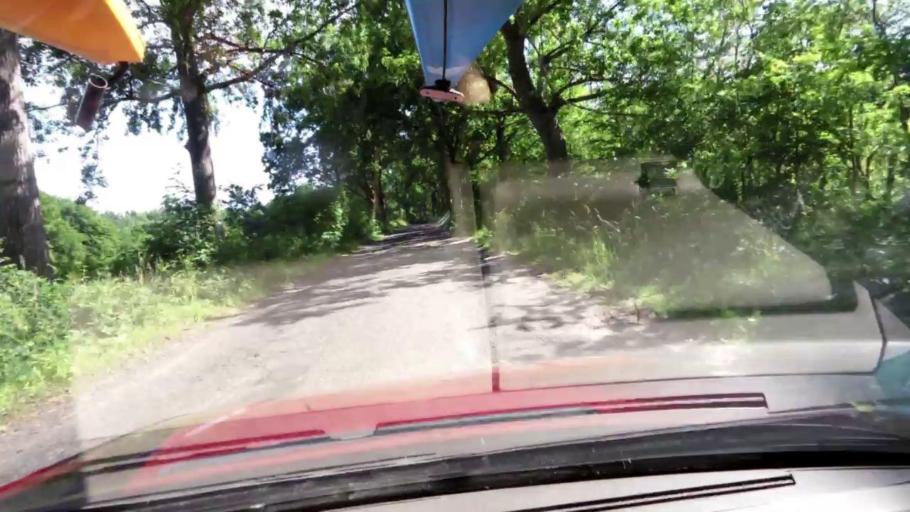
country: PL
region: Pomeranian Voivodeship
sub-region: Powiat slupski
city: Kepice
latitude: 54.1917
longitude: 16.8883
